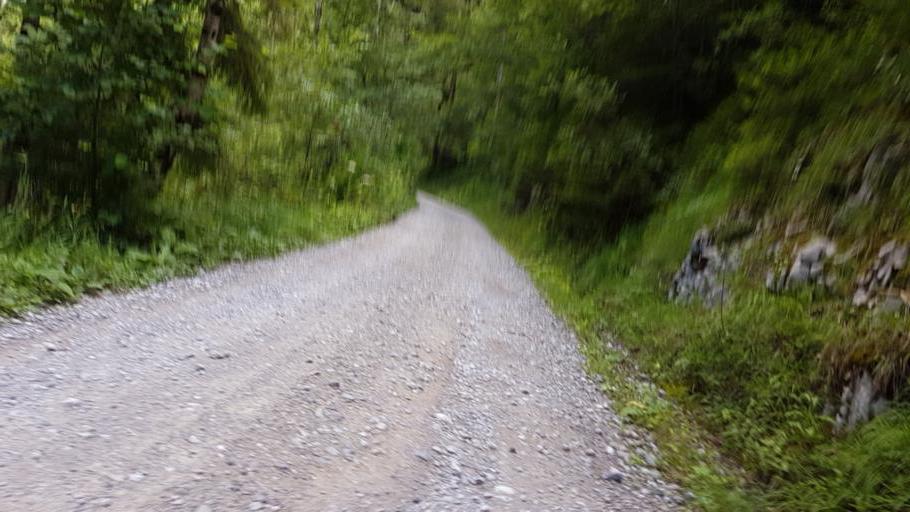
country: CH
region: Bern
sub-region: Obersimmental-Saanen District
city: Boltigen
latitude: 46.6780
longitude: 7.4507
